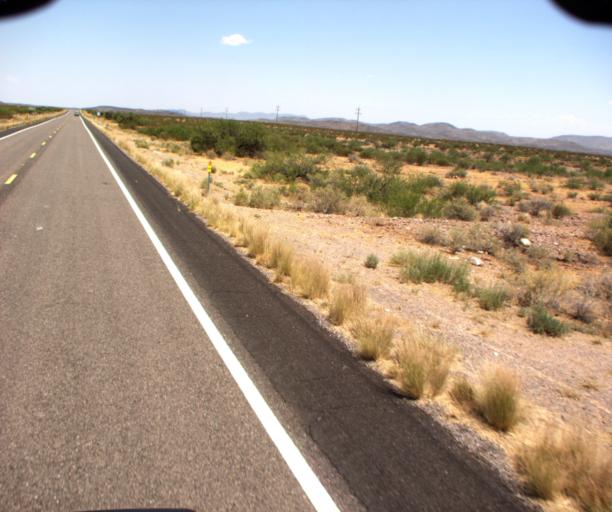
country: US
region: Arizona
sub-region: Graham County
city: Swift Trail Junction
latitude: 32.7628
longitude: -109.4472
